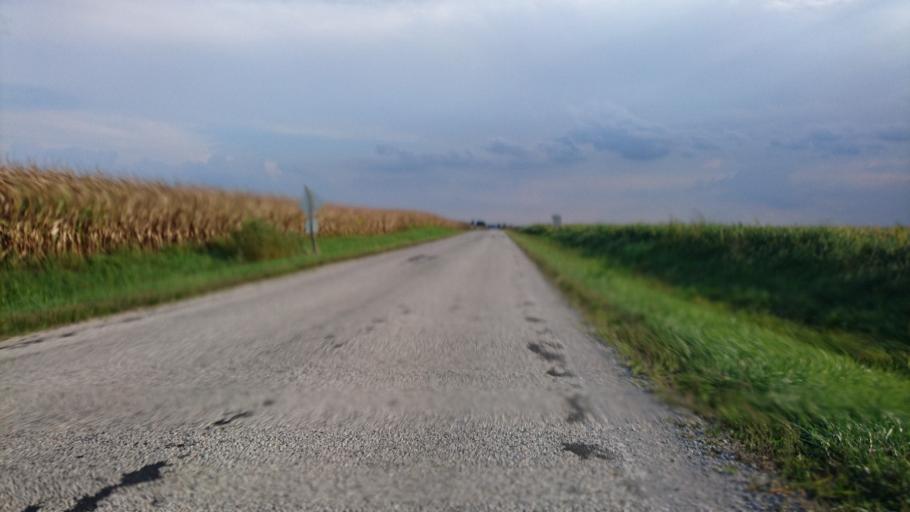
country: US
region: Illinois
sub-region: Logan County
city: Atlanta
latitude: 40.2570
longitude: -89.2052
